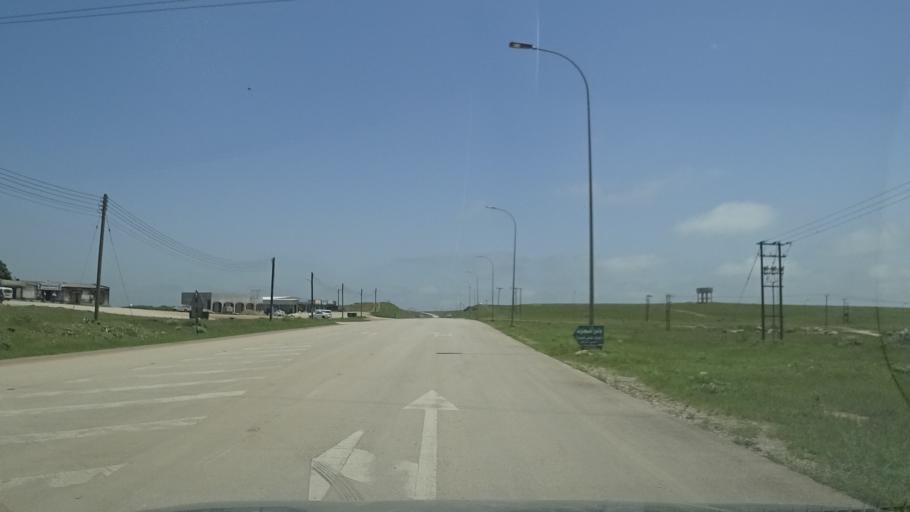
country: OM
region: Zufar
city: Salalah
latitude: 17.2403
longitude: 54.2847
